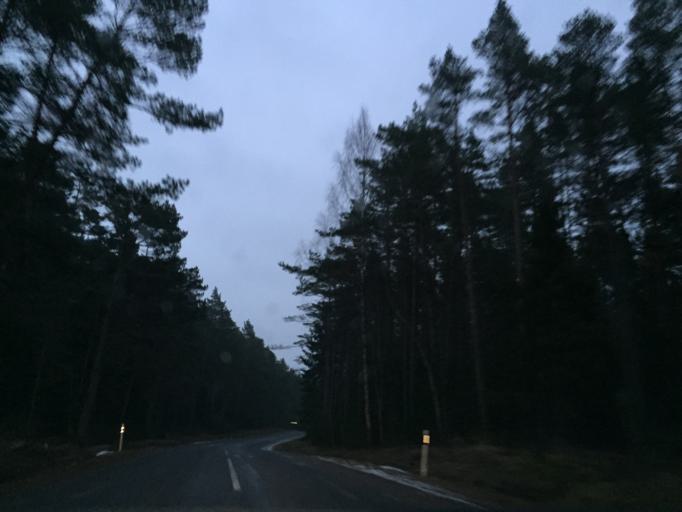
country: EE
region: Saare
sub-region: Kuressaare linn
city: Kuressaare
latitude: 58.5896
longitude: 22.6088
